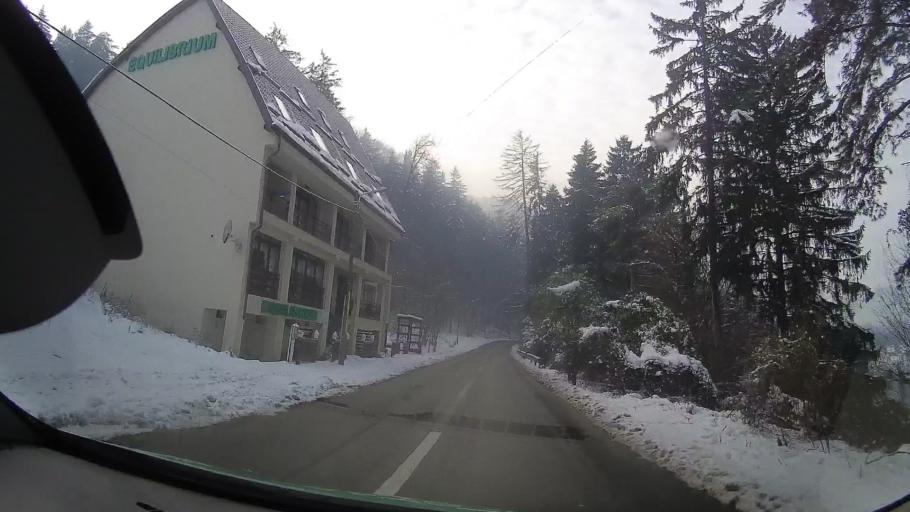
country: RO
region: Neamt
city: Piatra Neamt
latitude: 46.9240
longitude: 26.3594
